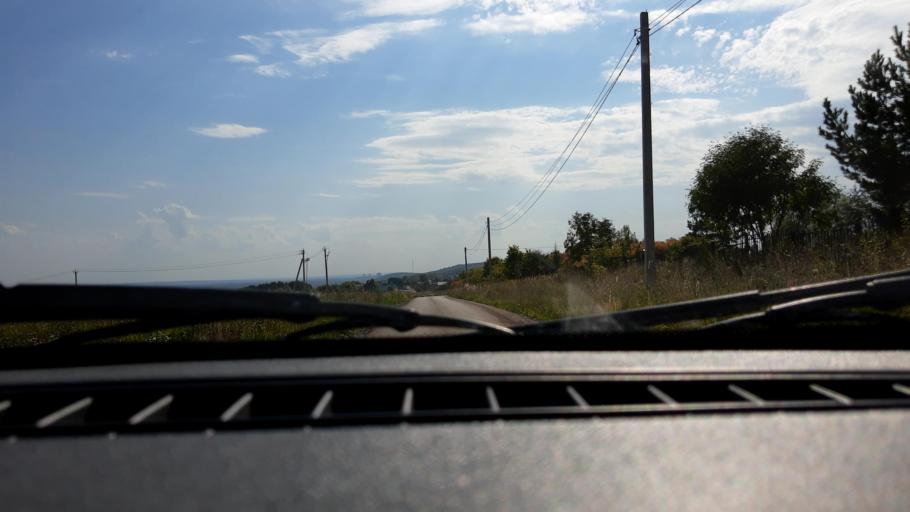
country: RU
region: Bashkortostan
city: Ufa
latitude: 54.8494
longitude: 56.1620
